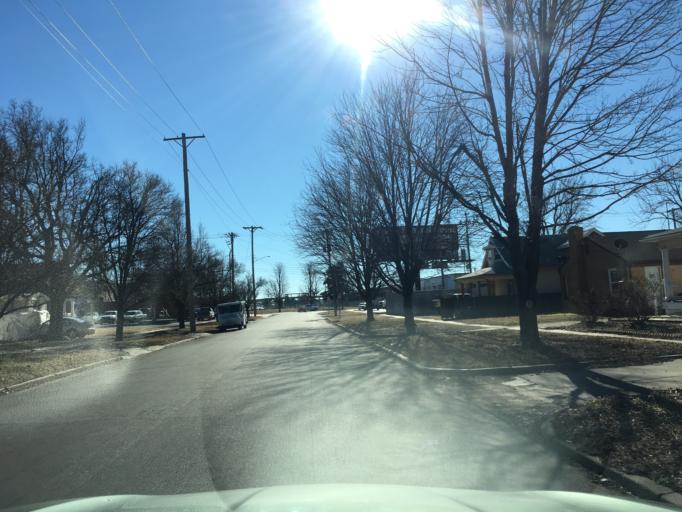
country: US
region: Kansas
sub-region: Sedgwick County
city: Wichita
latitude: 37.6876
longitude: -97.3121
